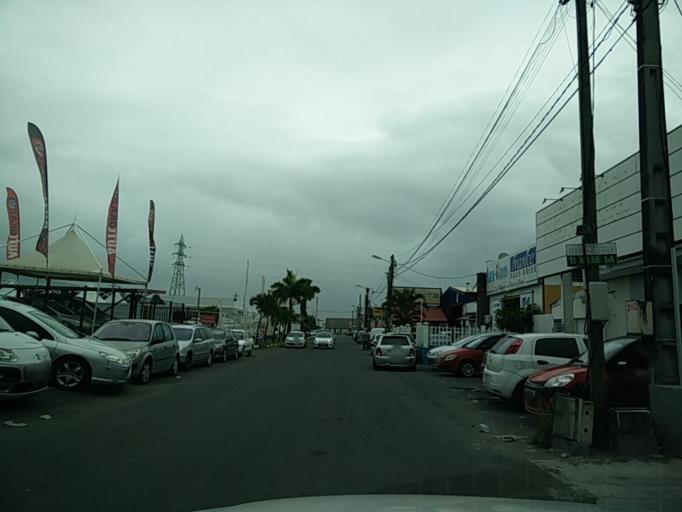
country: GP
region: Guadeloupe
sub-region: Guadeloupe
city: Pointe-a-Pitre
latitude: 16.2531
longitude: -61.5563
